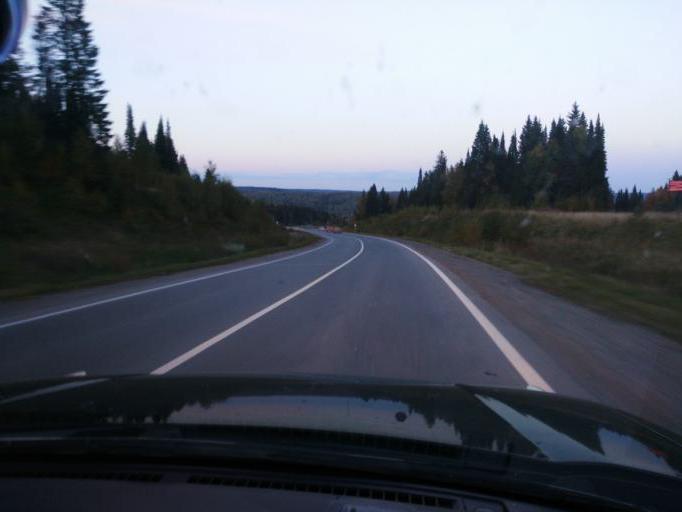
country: RU
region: Perm
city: Sylva
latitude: 58.2921
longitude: 56.8340
